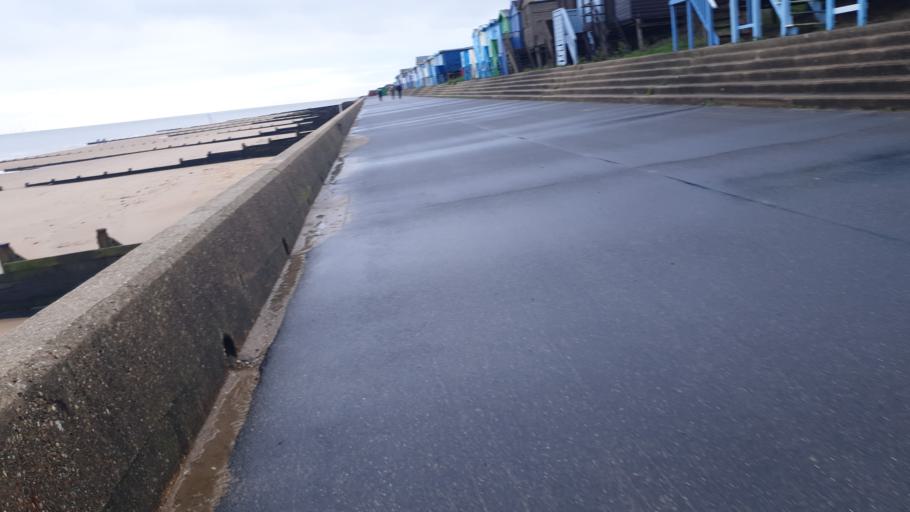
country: GB
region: England
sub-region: Essex
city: Walton-on-the-Naze
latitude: 51.8395
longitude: 1.2613
